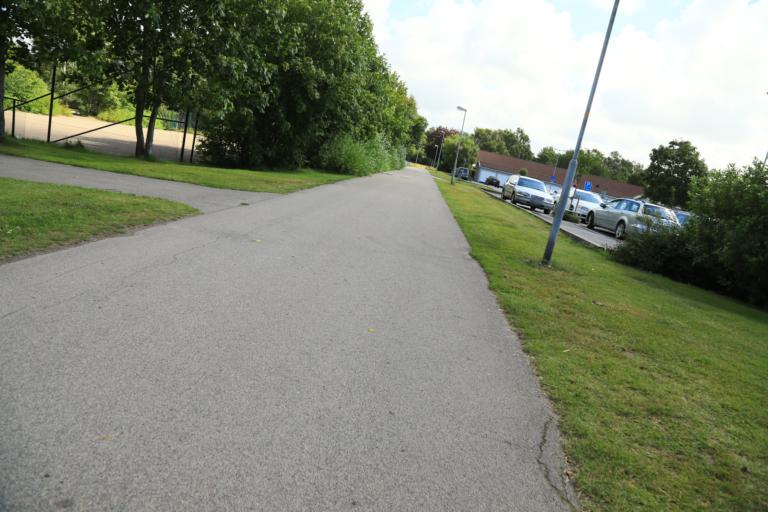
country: SE
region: Halland
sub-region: Varbergs Kommun
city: Varberg
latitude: 57.1148
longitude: 12.2877
